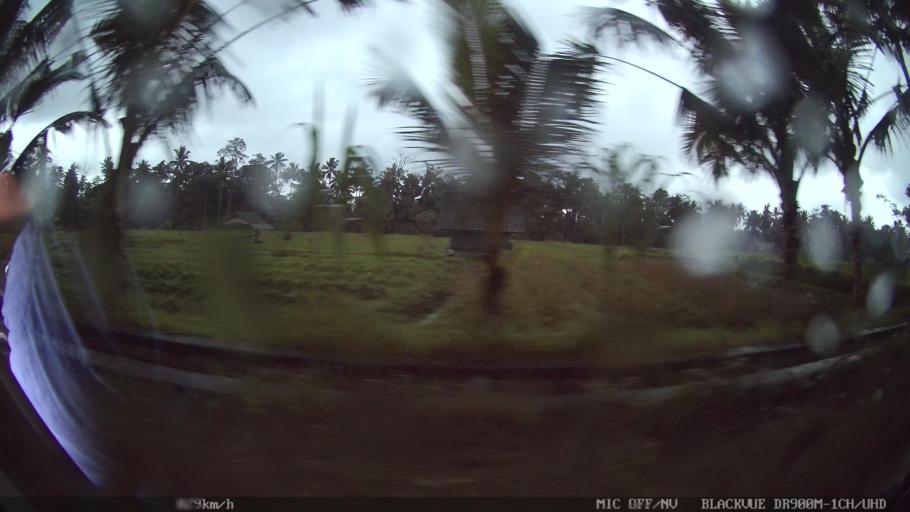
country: ID
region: Bali
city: Kekeran
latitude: -8.4862
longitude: 115.1872
